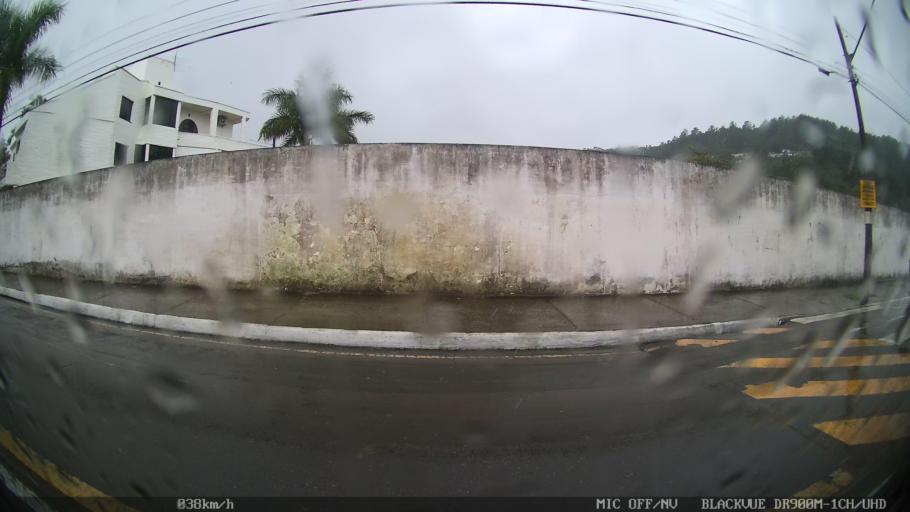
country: BR
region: Santa Catarina
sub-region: Balneario Camboriu
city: Balneario Camboriu
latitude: -27.0096
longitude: -48.6242
